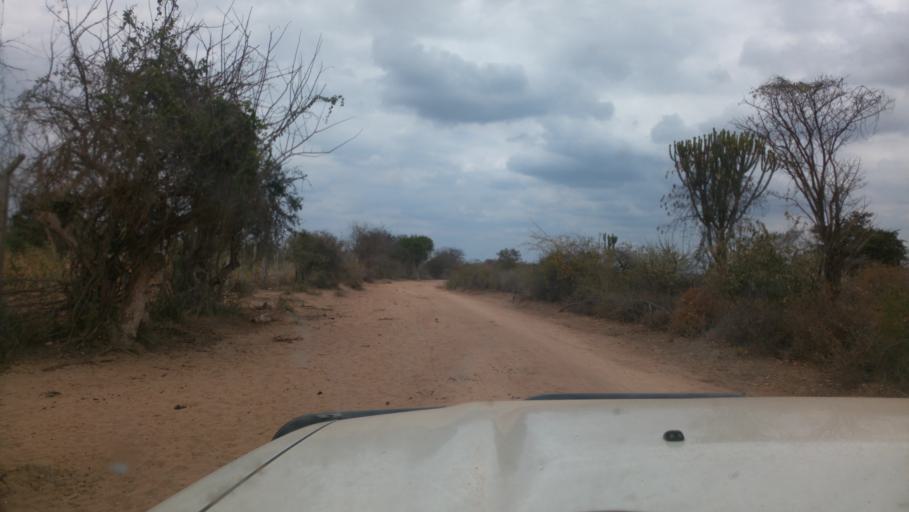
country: KE
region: Kitui
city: Kitui
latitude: -1.8176
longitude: 38.4289
